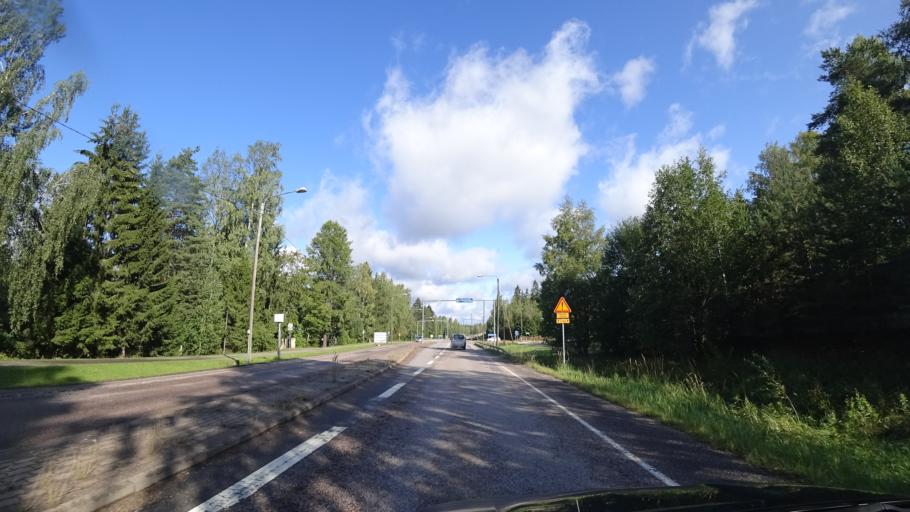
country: FI
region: Uusimaa
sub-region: Helsinki
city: Tuusula
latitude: 60.4142
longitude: 25.0022
